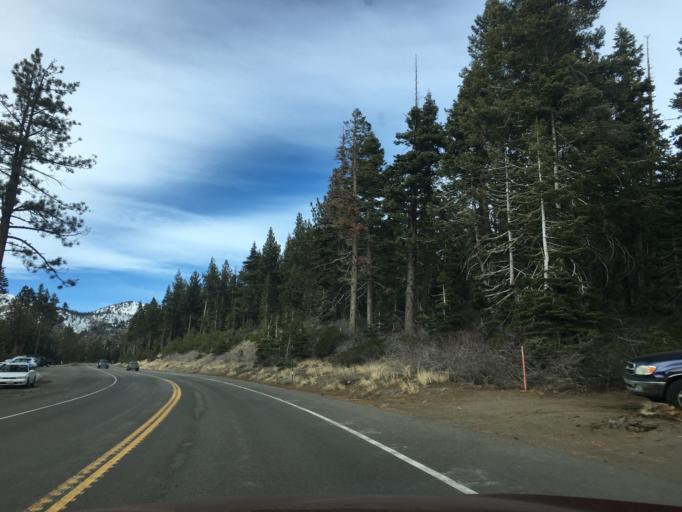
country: US
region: Nevada
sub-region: Washoe County
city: Incline Village
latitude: 39.2672
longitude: -119.9300
